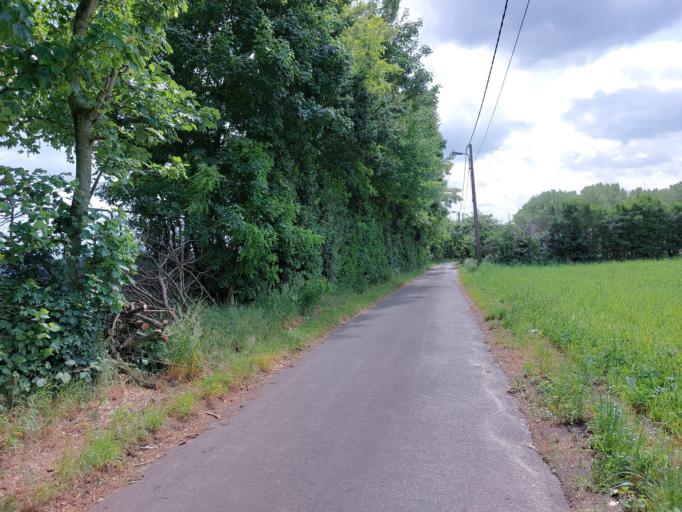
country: BE
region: Wallonia
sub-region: Province du Hainaut
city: Saint-Ghislain
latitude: 50.4857
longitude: 3.8004
